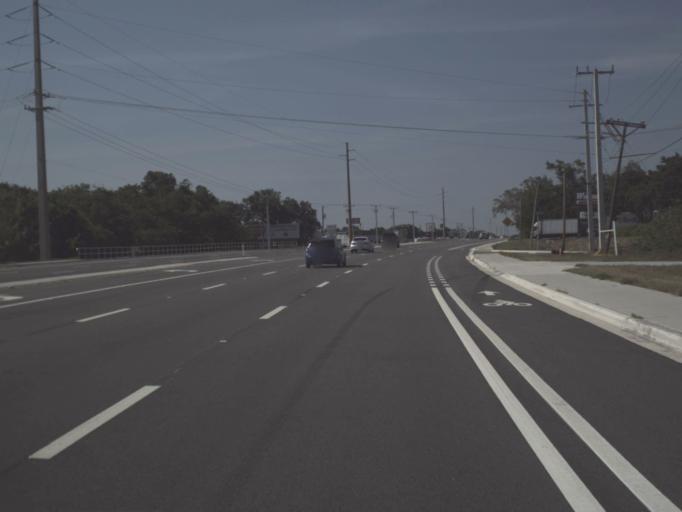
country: US
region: Florida
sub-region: Brevard County
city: Cocoa
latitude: 28.4051
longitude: -80.7550
